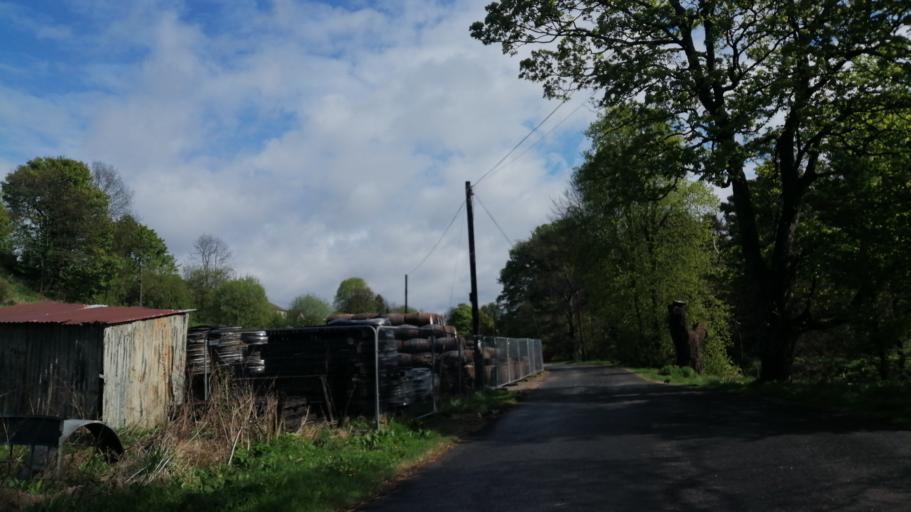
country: GB
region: Scotland
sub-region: Moray
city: Keith
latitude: 57.5415
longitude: -2.9611
